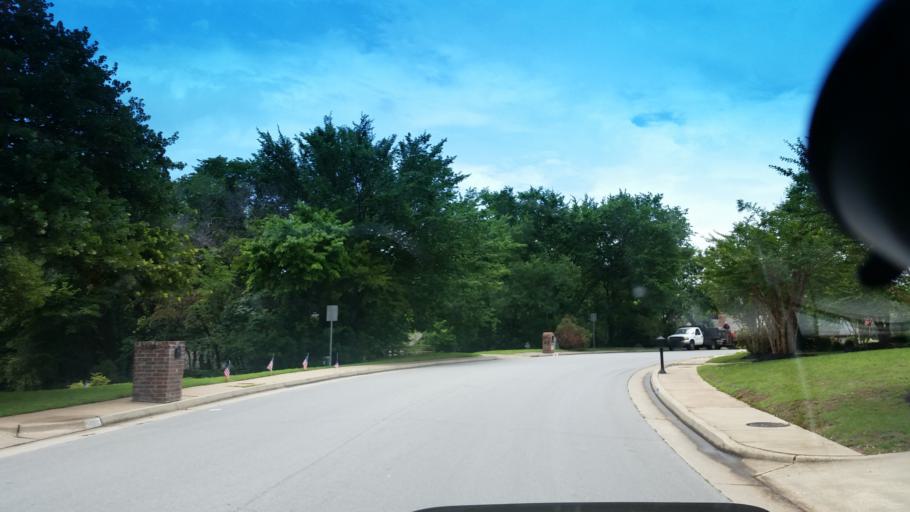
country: US
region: Oklahoma
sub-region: Oklahoma County
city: Edmond
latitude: 35.6391
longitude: -97.4322
